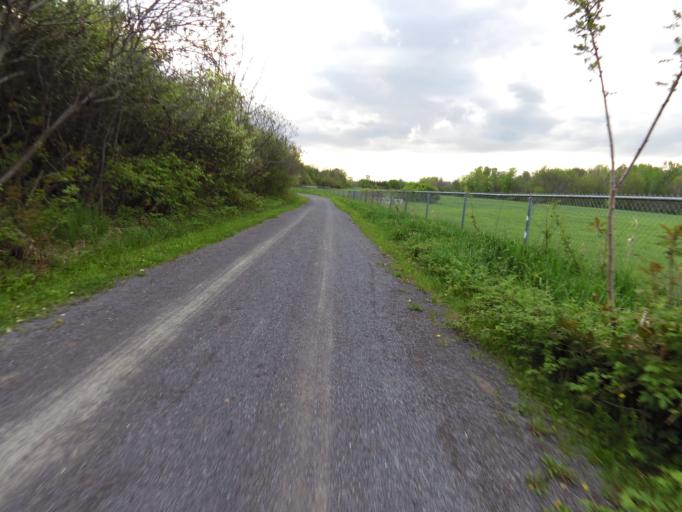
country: CA
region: Ontario
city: Bells Corners
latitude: 45.3364
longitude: -75.8612
